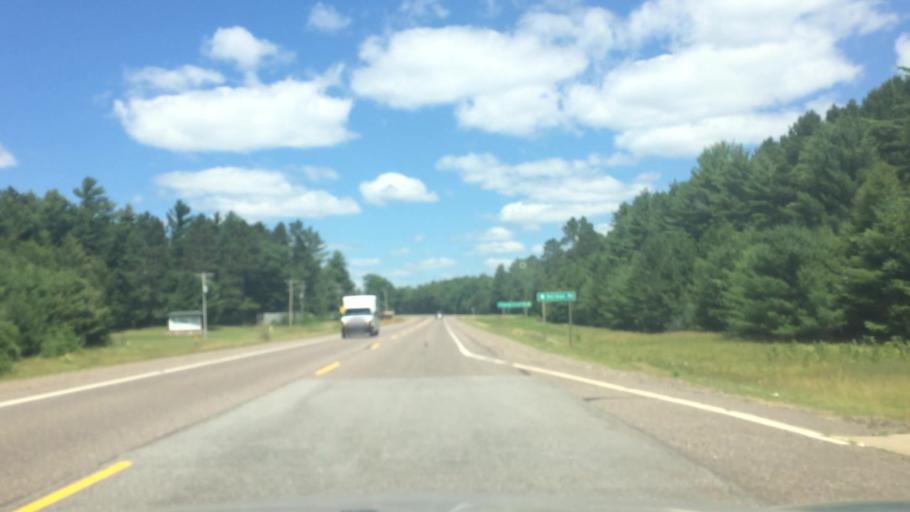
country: US
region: Wisconsin
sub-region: Vilas County
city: Lac du Flambeau
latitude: 45.9374
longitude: -89.6966
